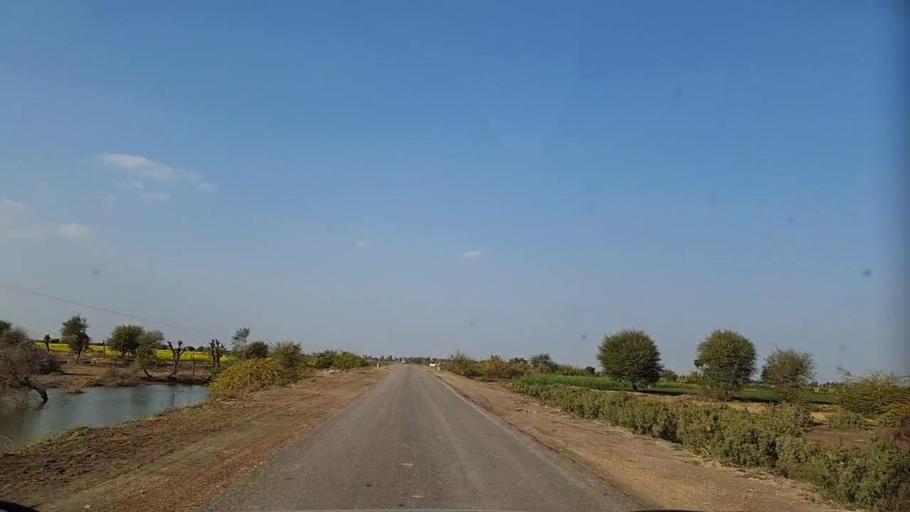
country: PK
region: Sindh
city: Pithoro
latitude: 25.7039
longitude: 69.2220
